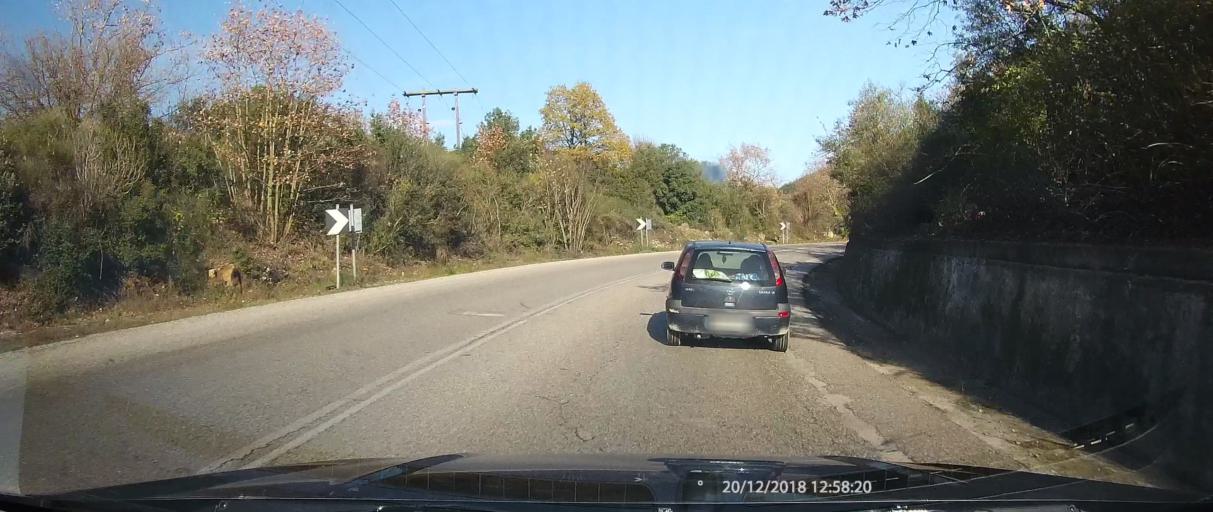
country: GR
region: West Greece
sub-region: Nomos Aitolias kai Akarnanias
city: Pappadhatai
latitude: 38.5356
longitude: 21.3755
